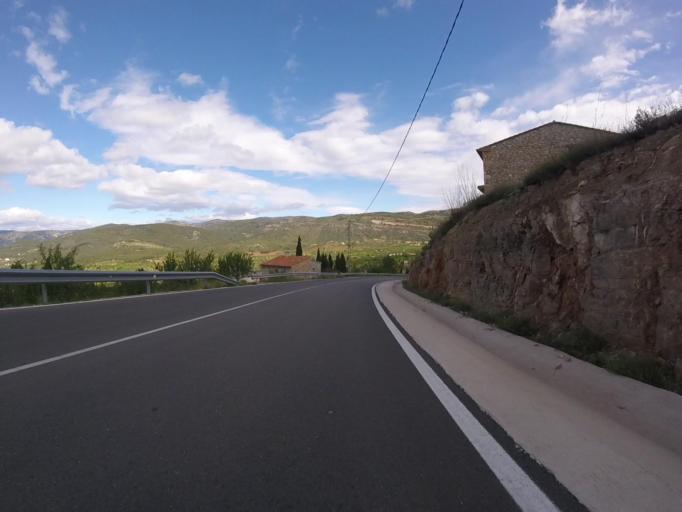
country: ES
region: Valencia
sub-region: Provincia de Castello
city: Culla
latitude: 40.2751
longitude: -0.1111
